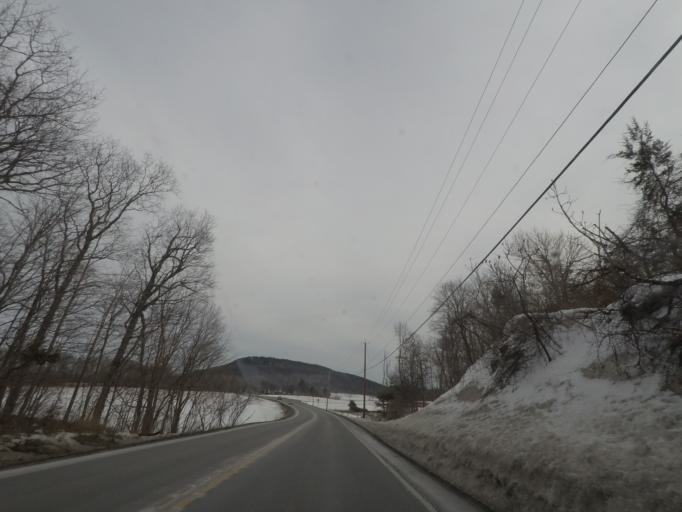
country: US
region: New York
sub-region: Albany County
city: Voorheesville
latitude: 42.5774
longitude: -73.9764
